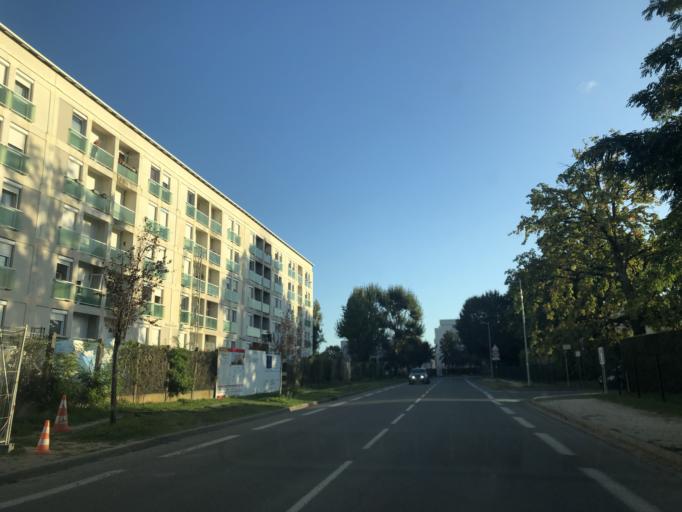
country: FR
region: Aquitaine
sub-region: Departement de la Gironde
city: Merignac
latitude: 44.8459
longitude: -0.6352
